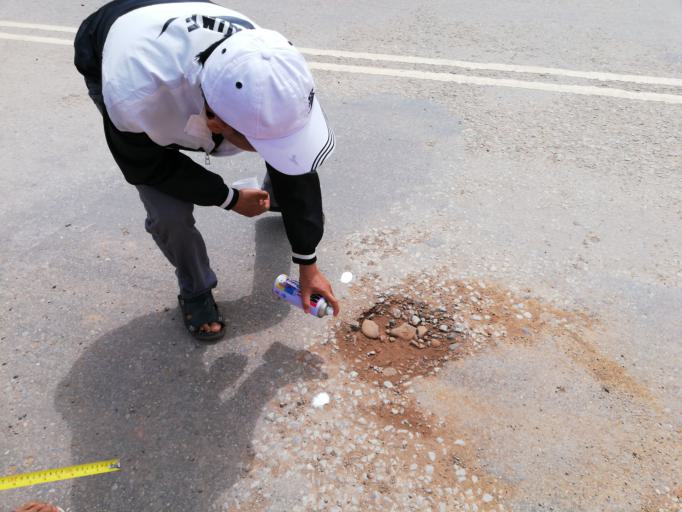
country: LA
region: Loungnamtha
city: Louang Namtha
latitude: 21.0024
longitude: 101.4075
